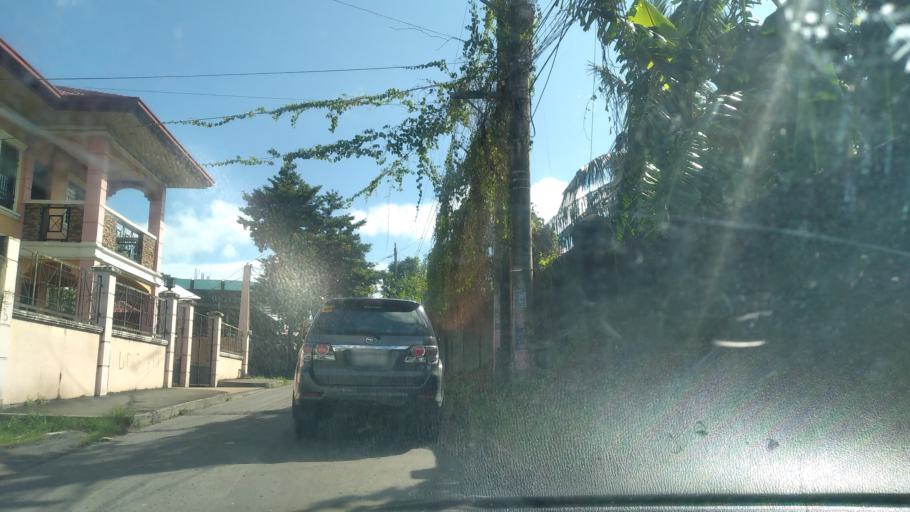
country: PH
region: Calabarzon
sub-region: Province of Quezon
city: Lucena
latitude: 13.9431
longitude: 121.6116
